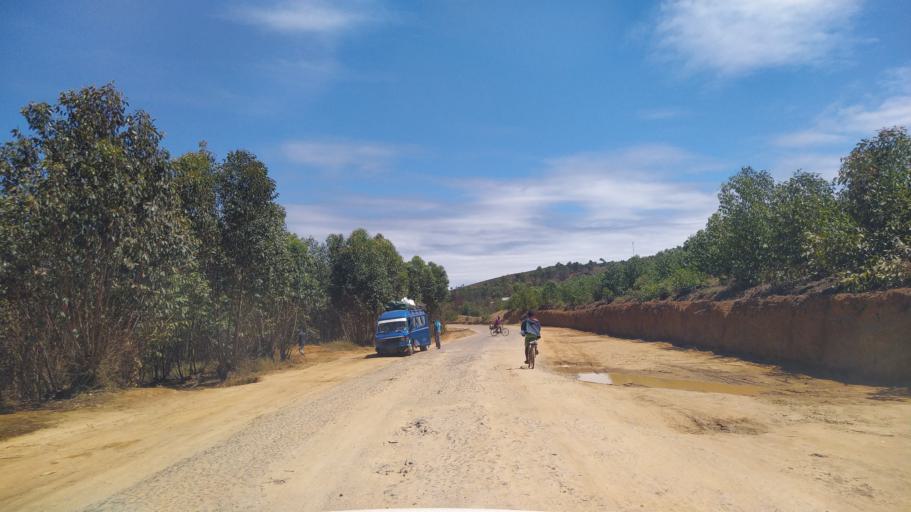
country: MG
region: Alaotra Mangoro
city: Moramanga
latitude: -18.7092
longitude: 48.2709
